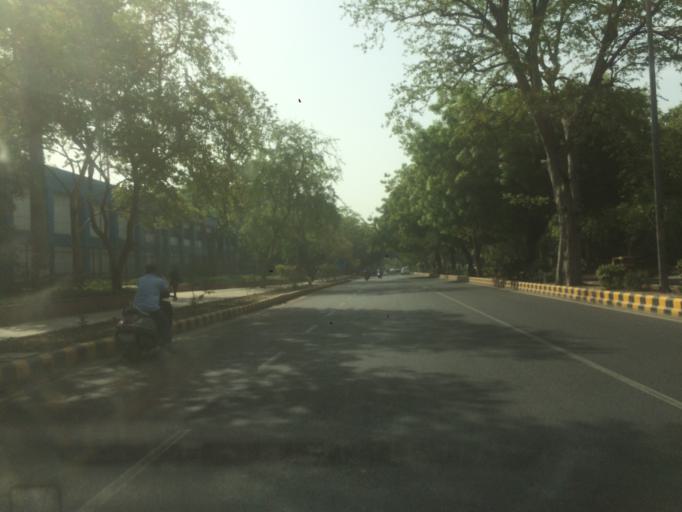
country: IN
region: NCT
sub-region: Central Delhi
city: Karol Bagh
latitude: 28.6260
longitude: 77.1970
